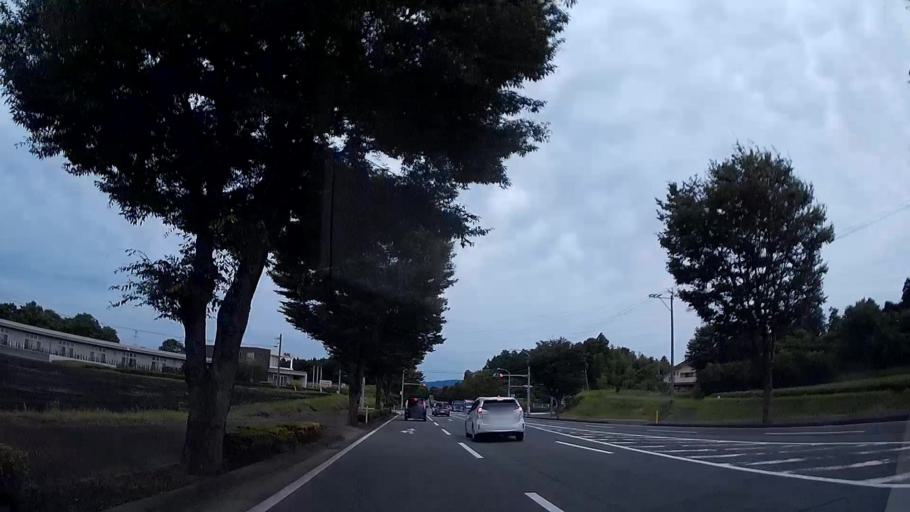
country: JP
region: Kumamoto
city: Ozu
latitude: 32.9155
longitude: 130.8404
